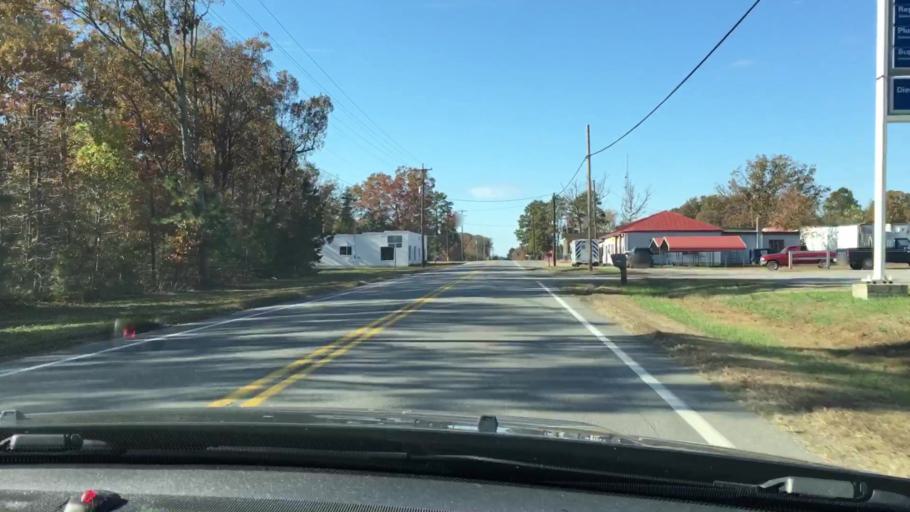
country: US
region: Virginia
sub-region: King William County
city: Central Garage
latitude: 37.7174
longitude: -77.0725
